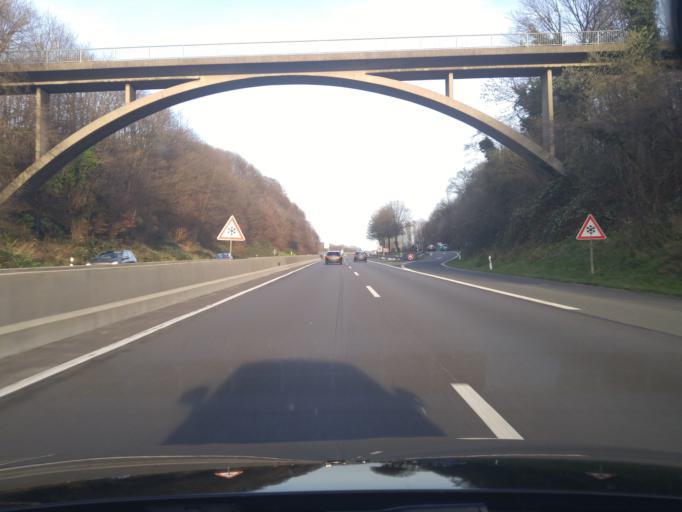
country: DE
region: North Rhine-Westphalia
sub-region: Regierungsbezirk Dusseldorf
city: Muelheim (Ruhr)
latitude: 51.3716
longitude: 6.8891
